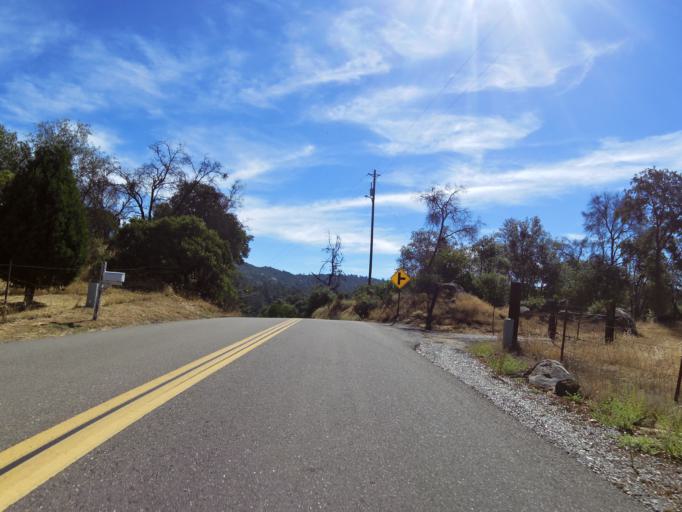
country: US
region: California
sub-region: Mariposa County
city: Mariposa
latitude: 37.4283
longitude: -119.9486
